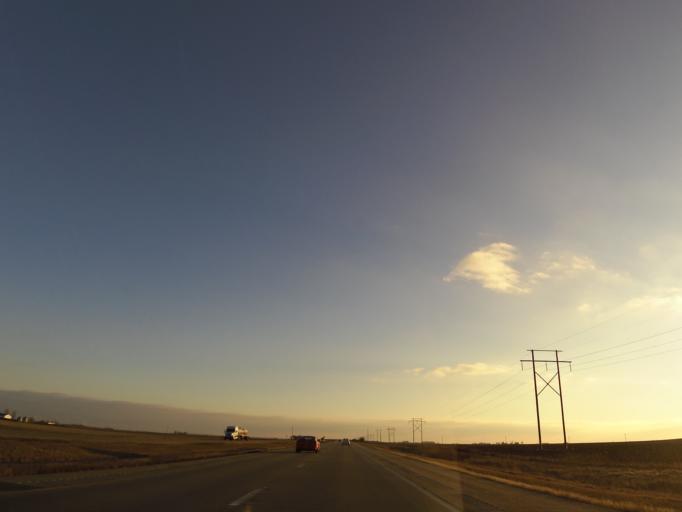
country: US
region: Illinois
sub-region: Woodford County
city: Minonk
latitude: 40.9743
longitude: -89.0566
